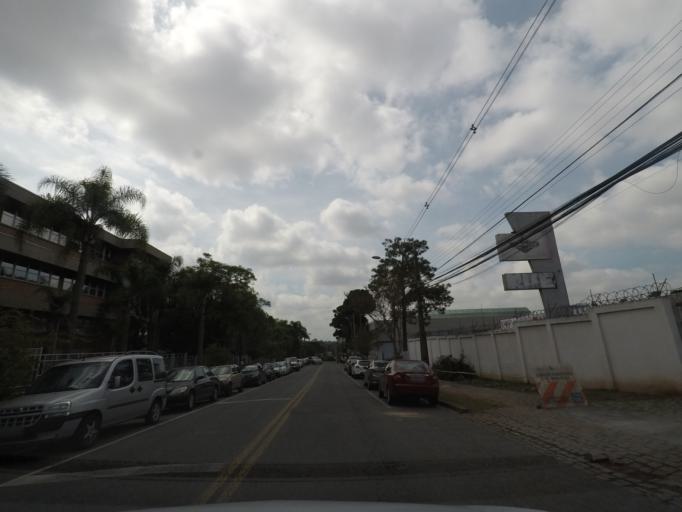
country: BR
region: Parana
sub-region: Curitiba
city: Curitiba
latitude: -25.4567
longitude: -49.2572
